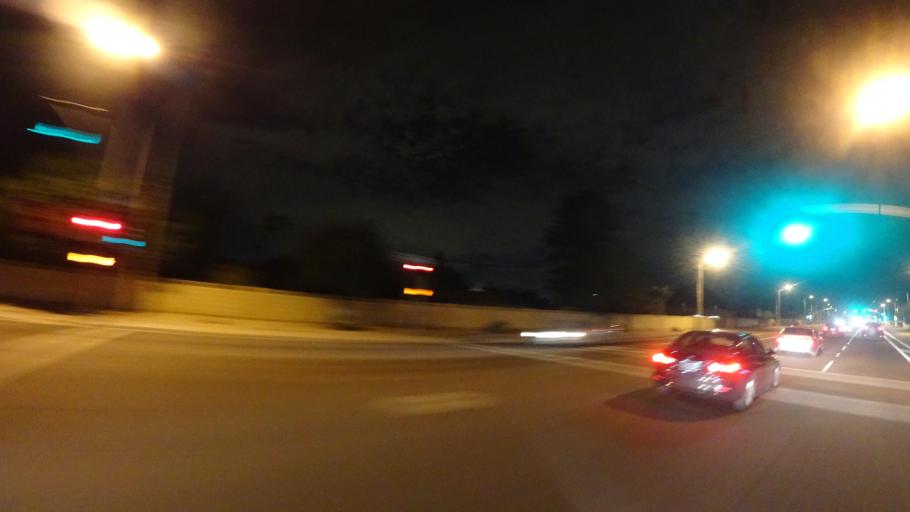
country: US
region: Arizona
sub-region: Maricopa County
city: Tempe
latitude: 33.3965
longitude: -111.9091
